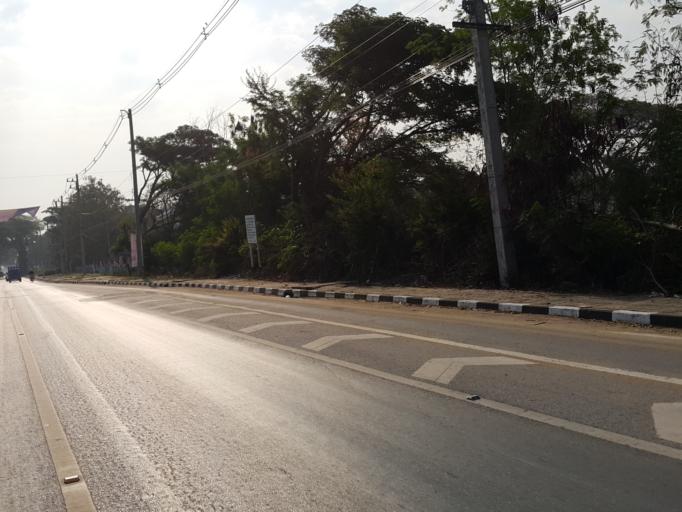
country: TH
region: Chiang Mai
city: San Kamphaeng
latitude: 18.7552
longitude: 99.0986
